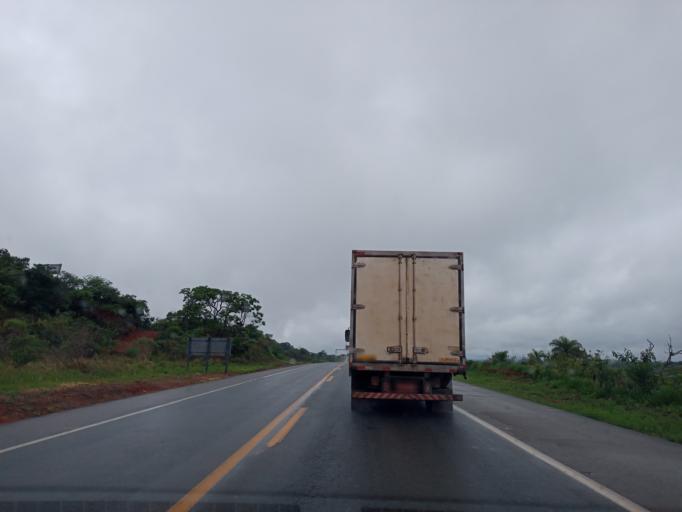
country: BR
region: Minas Gerais
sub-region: Campos Altos
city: Campos Altos
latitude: -19.7415
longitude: -46.0058
